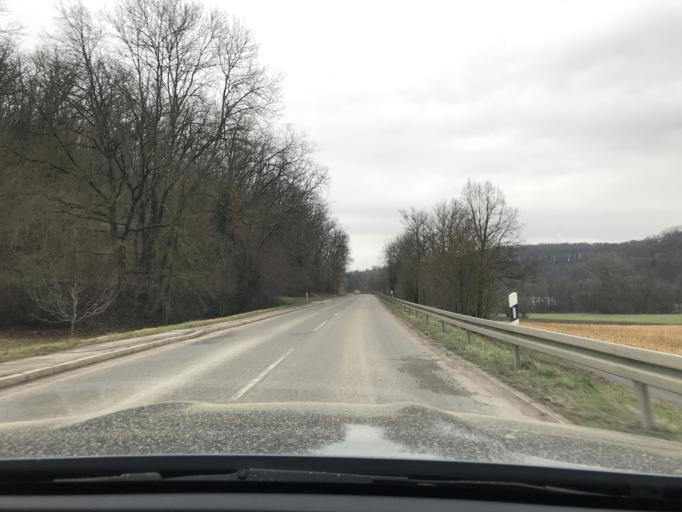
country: DE
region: Baden-Wuerttemberg
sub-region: Regierungsbezirk Stuttgart
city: Kirchberg an der Murr
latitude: 48.9463
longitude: 9.3222
